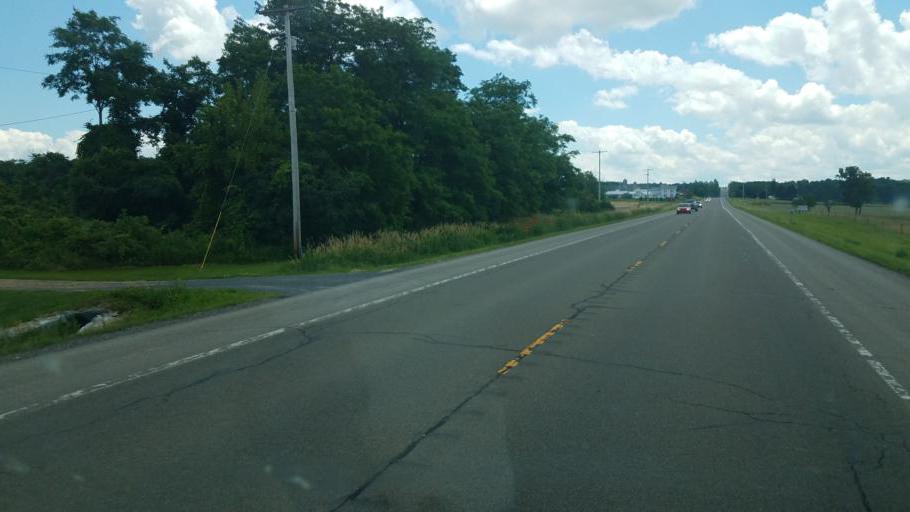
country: US
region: New York
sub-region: Yates County
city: Keuka Park
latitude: 42.6059
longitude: -77.0379
